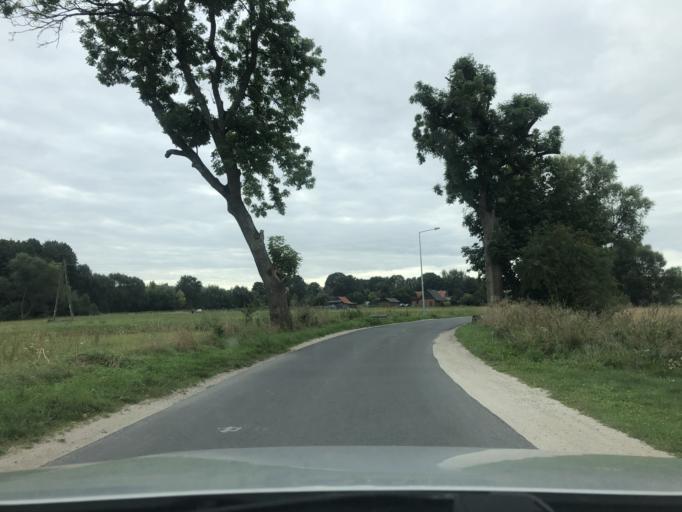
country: PL
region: Greater Poland Voivodeship
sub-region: Powiat pilski
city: Pila
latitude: 53.2690
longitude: 16.6902
